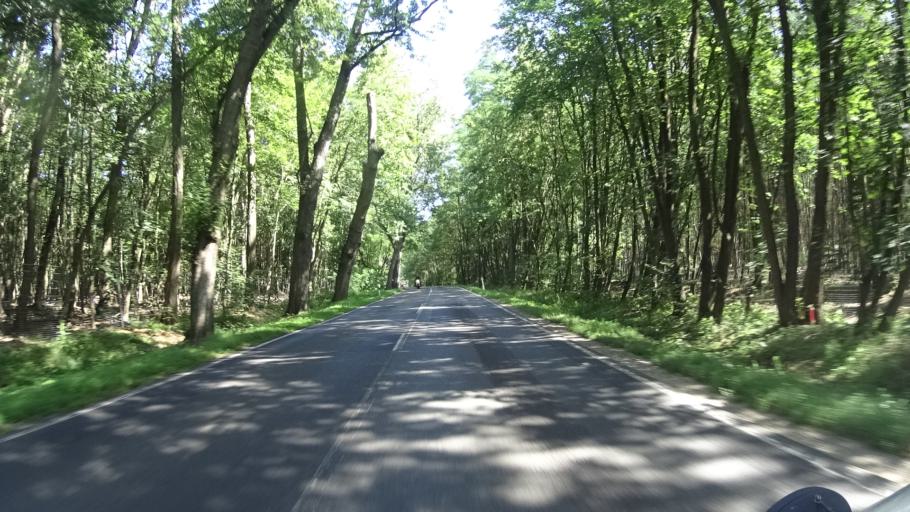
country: DE
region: Brandenburg
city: Fichtenwalde
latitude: 52.3143
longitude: 12.8783
